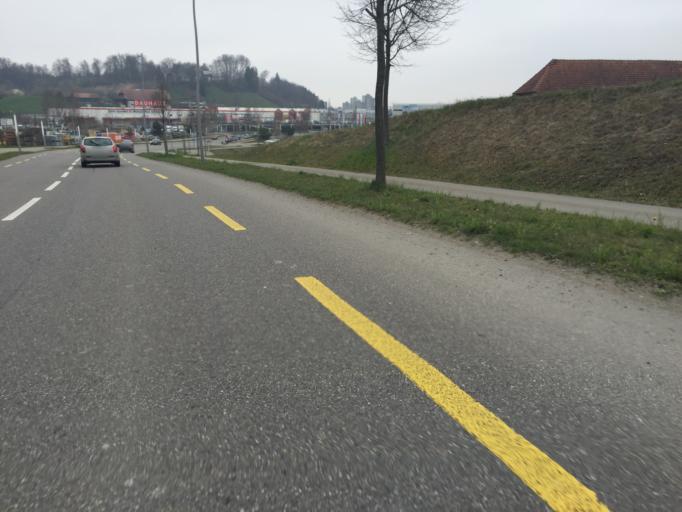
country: CH
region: Bern
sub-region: Bern-Mittelland District
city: Koniz
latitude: 46.9289
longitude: 7.3766
